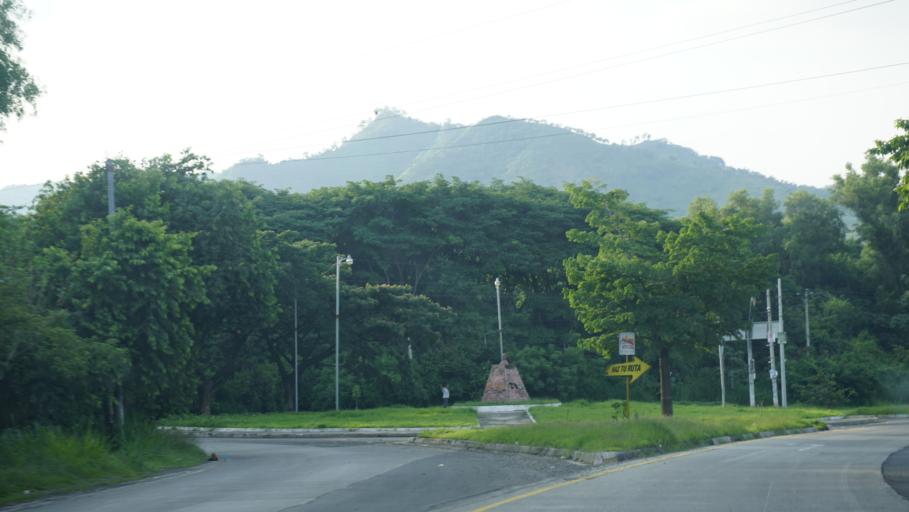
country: SV
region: Santa Ana
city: Santa Ana
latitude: 14.0108
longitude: -89.5429
